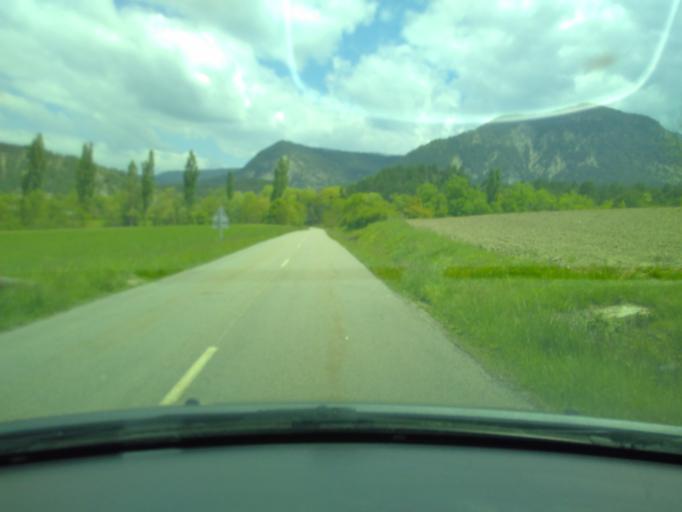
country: FR
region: Rhone-Alpes
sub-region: Departement de la Drome
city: Die
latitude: 44.6482
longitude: 5.4490
